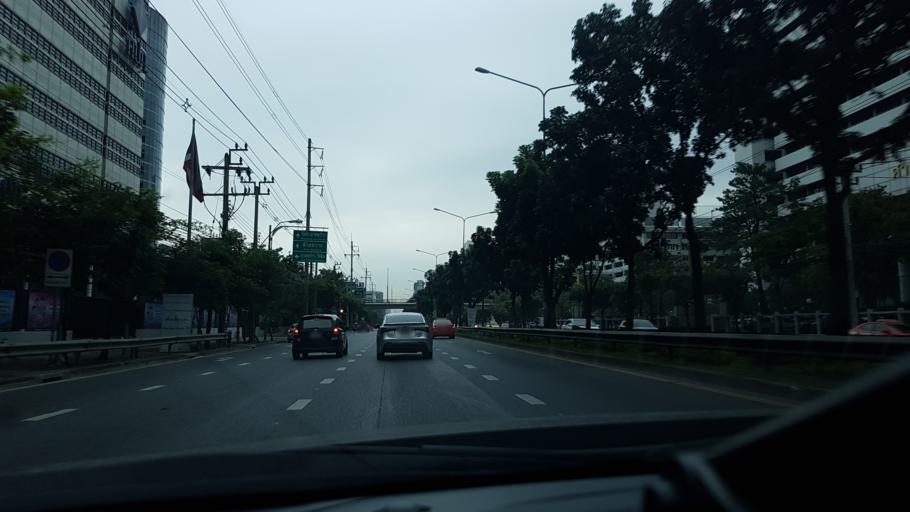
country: TH
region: Bangkok
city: Chatuchak
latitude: 13.8168
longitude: 100.5756
